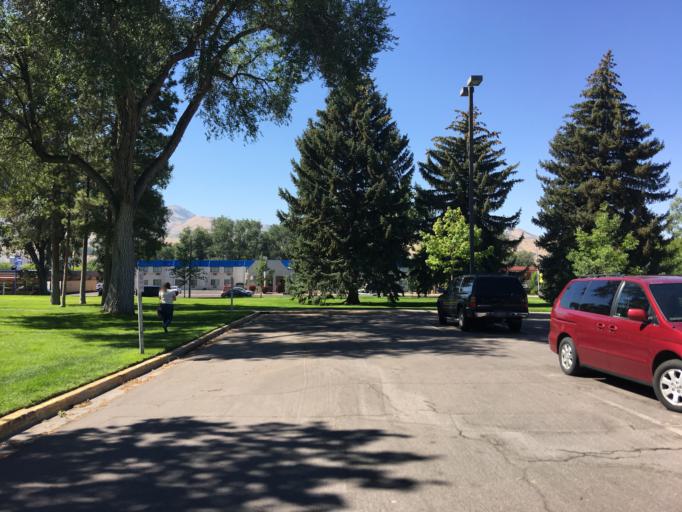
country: US
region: Idaho
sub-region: Bannock County
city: Pocatello
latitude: 42.8616
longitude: -112.4363
